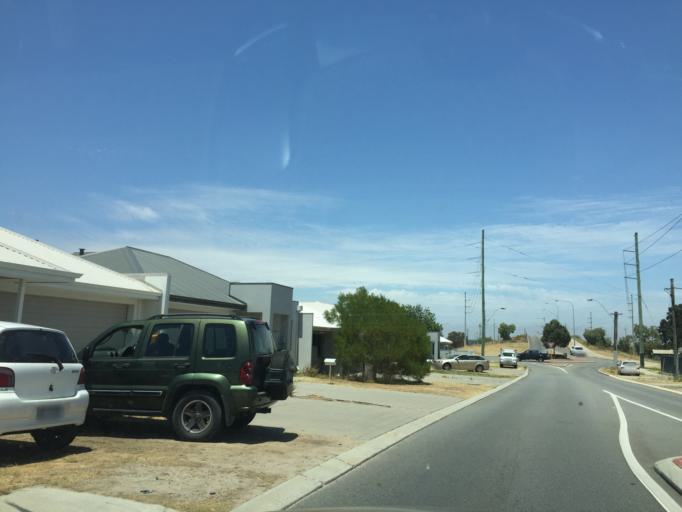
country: AU
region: Western Australia
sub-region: Canning
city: Cannington
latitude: -32.0140
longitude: 115.9489
